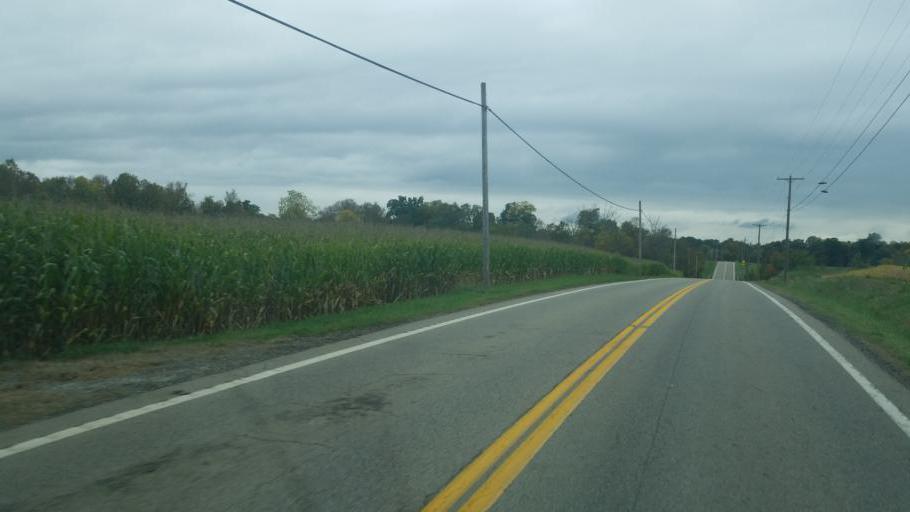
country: US
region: Ohio
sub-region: Richland County
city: Lincoln Heights
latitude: 40.7121
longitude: -82.3890
